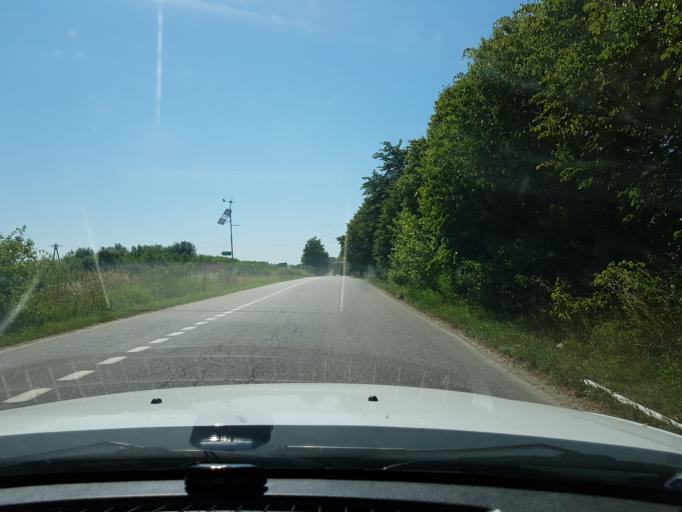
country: PL
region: West Pomeranian Voivodeship
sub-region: Powiat koszalinski
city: Mielno
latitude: 54.2089
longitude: 16.0660
